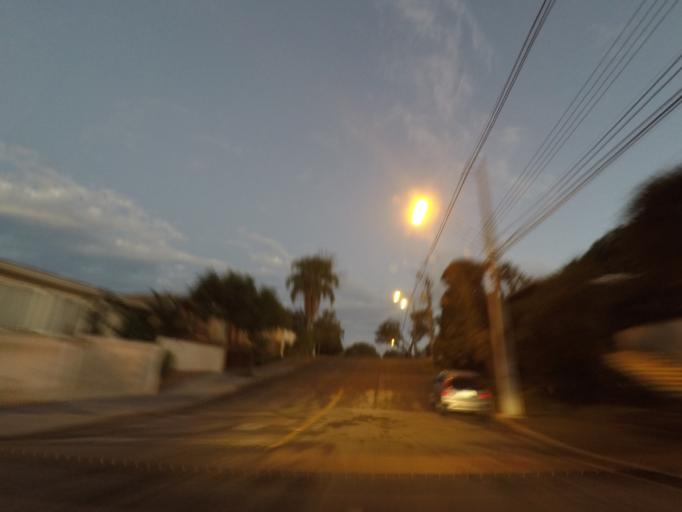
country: BR
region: Parana
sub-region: Curitiba
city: Curitiba
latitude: -25.4196
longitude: -49.2370
